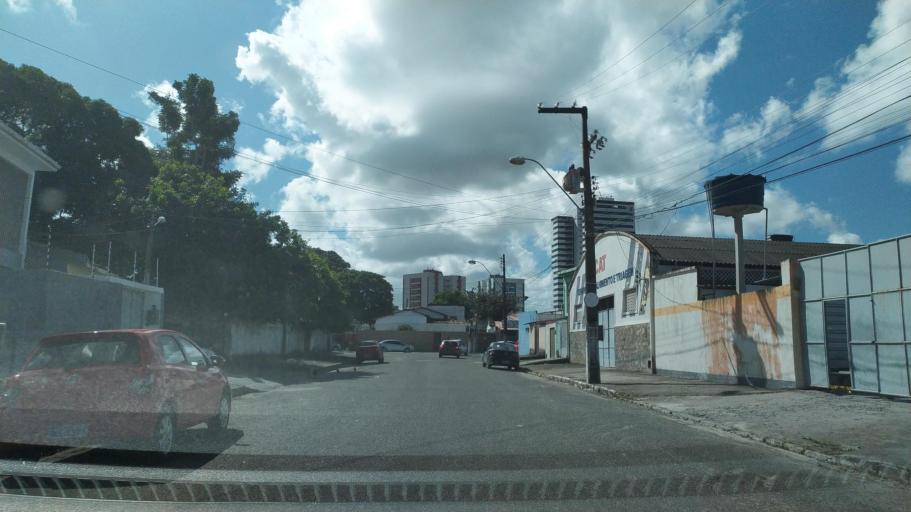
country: BR
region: Alagoas
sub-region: Maceio
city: Maceio
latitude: -9.6378
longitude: -35.7376
